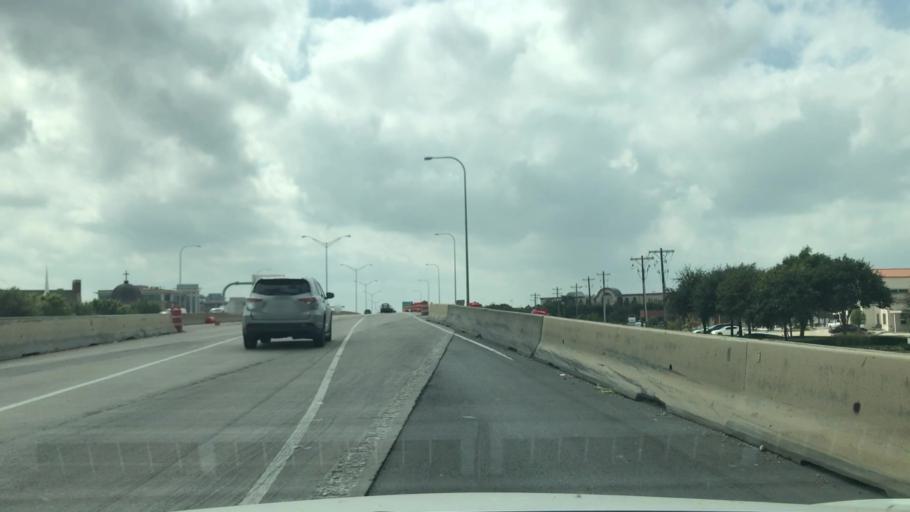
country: US
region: Texas
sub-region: Dallas County
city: Addison
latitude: 33.0378
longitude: -96.8298
